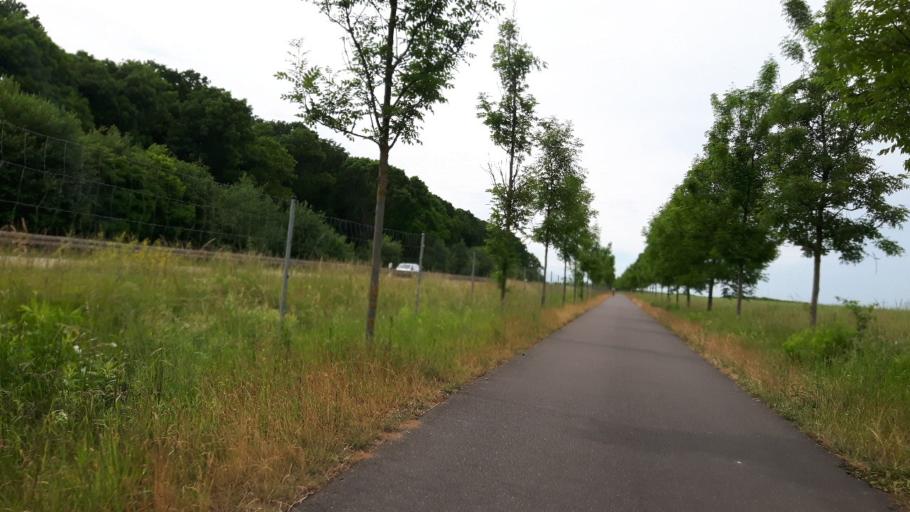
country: DE
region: Saxony
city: Rackwitz
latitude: 51.4017
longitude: 12.3316
